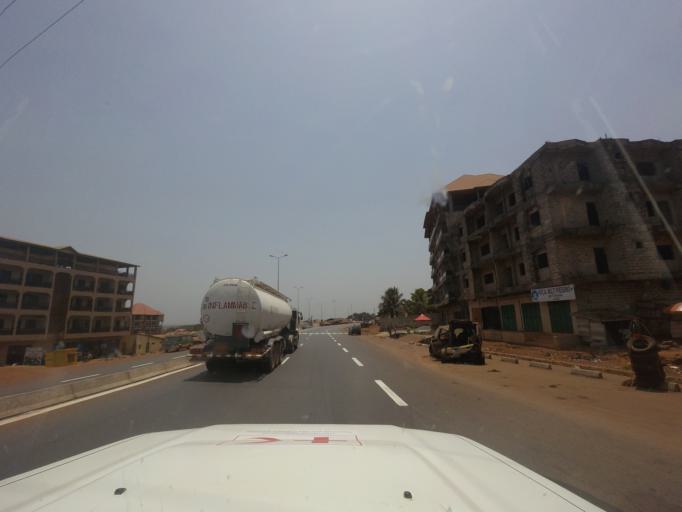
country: GN
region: Kindia
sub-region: Prefecture de Dubreka
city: Dubreka
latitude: 9.6764
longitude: -13.5169
